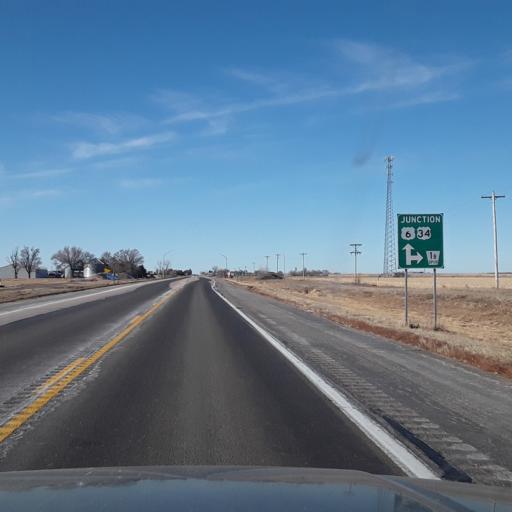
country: US
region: Nebraska
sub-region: Adams County
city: Hastings
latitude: 40.5681
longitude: -98.5023
